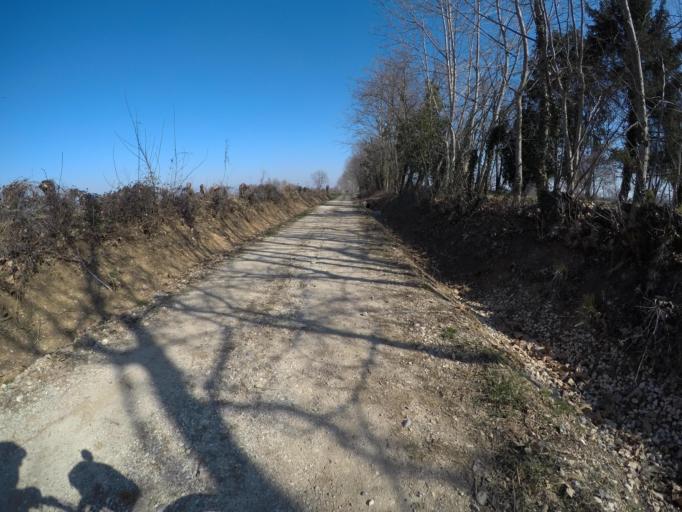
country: IT
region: Friuli Venezia Giulia
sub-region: Provincia di Udine
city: Lestizza
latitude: 45.9579
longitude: 13.1470
